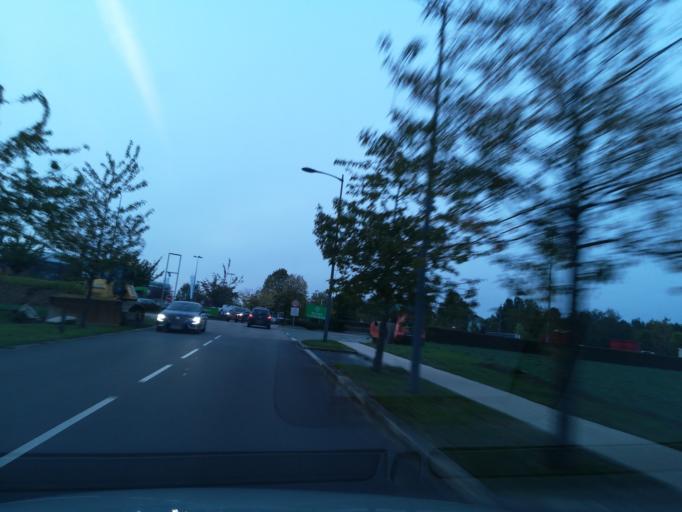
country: FR
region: Haute-Normandie
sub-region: Departement de la Seine-Maritime
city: Isneauville
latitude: 49.4878
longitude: 1.1459
